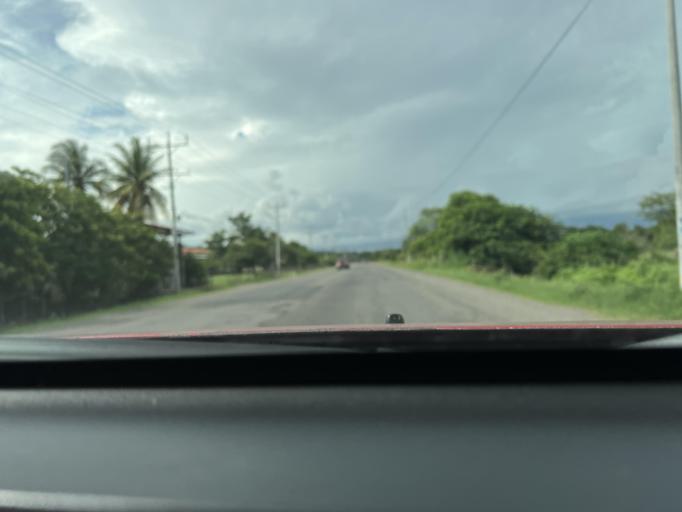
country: SV
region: La Union
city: San Alejo
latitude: 13.3865
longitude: -87.9041
